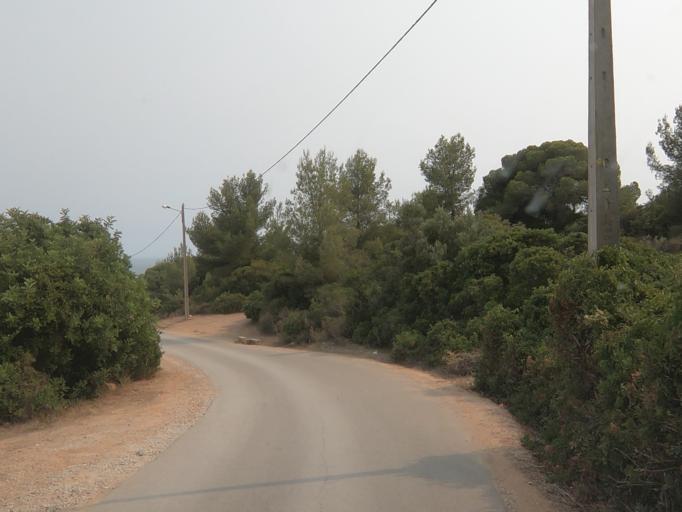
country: PT
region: Faro
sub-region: Silves
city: Armacao de Pera
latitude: 37.0936
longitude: -8.4009
